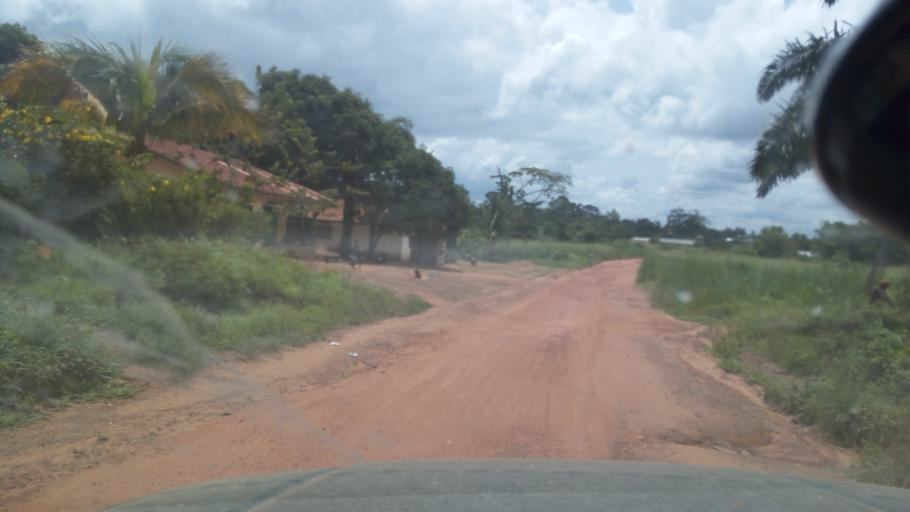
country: SL
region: Eastern Province
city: Kenema
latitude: 7.8764
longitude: -11.1619
